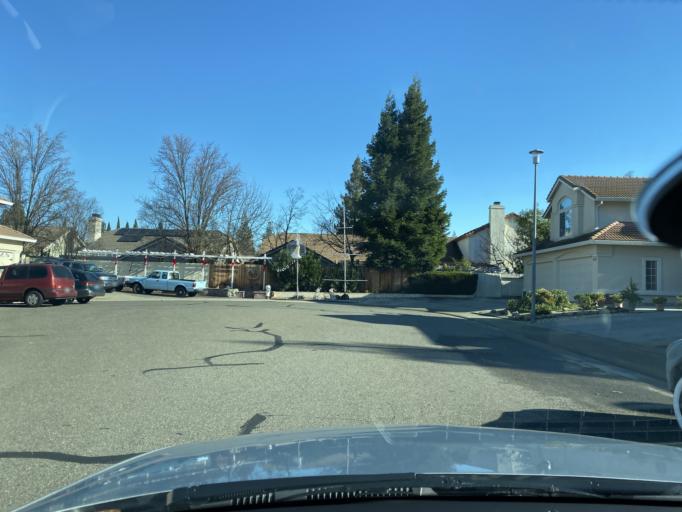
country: US
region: California
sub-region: Sacramento County
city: Elk Grove
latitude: 38.4317
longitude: -121.3824
